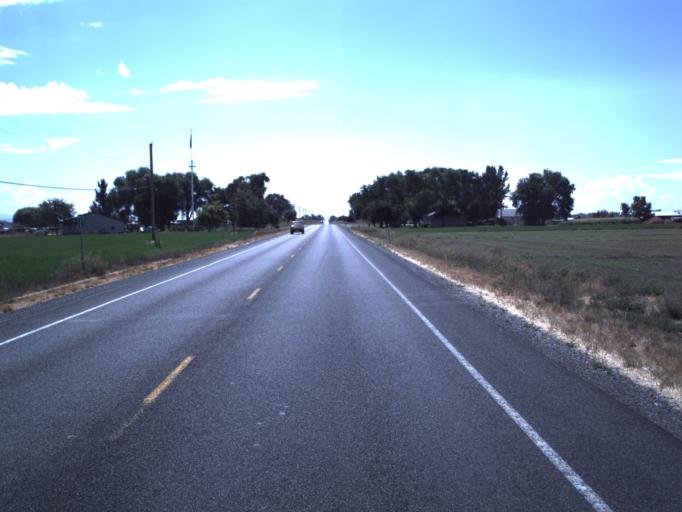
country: US
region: Utah
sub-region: Box Elder County
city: Honeyville
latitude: 41.5822
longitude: -112.1298
